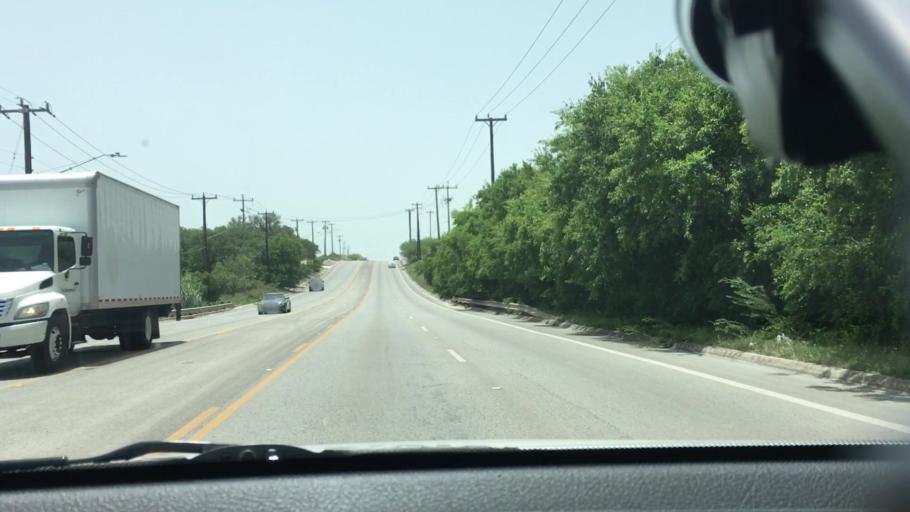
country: US
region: Texas
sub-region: Bexar County
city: Live Oak
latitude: 29.5597
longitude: -98.3511
